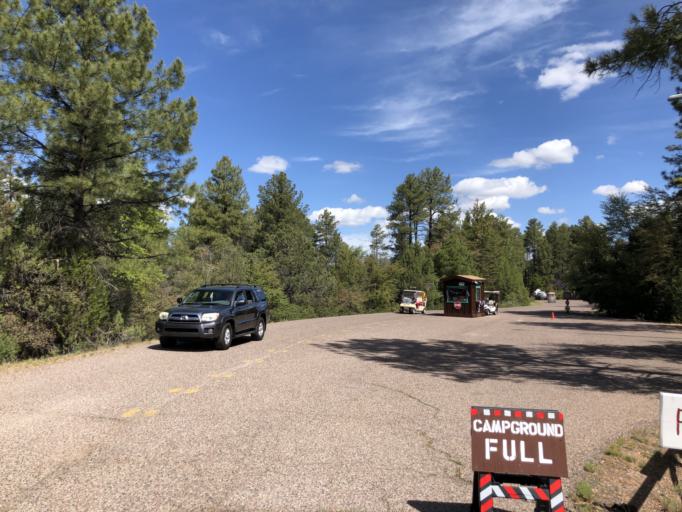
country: US
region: Arizona
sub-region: Gila County
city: Payson
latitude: 34.2696
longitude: -111.3191
